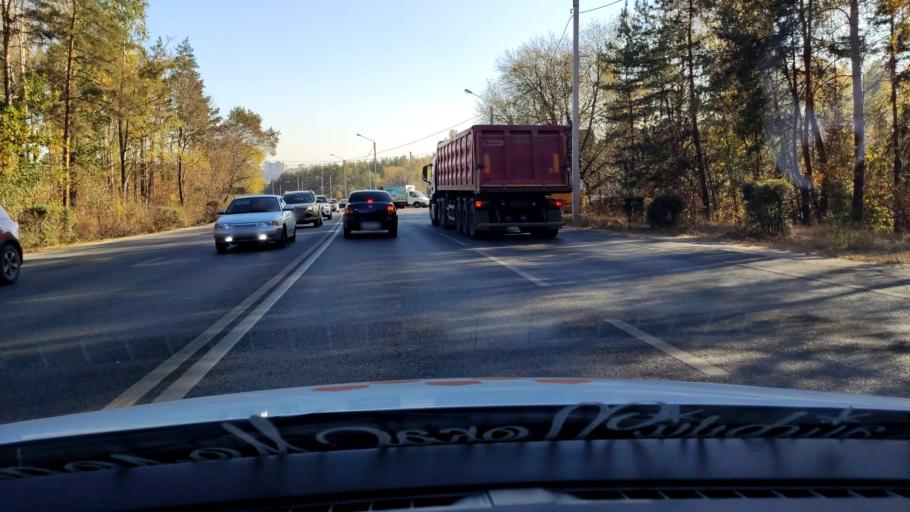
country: RU
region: Voronezj
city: Pridonskoy
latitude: 51.6763
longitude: 39.1152
